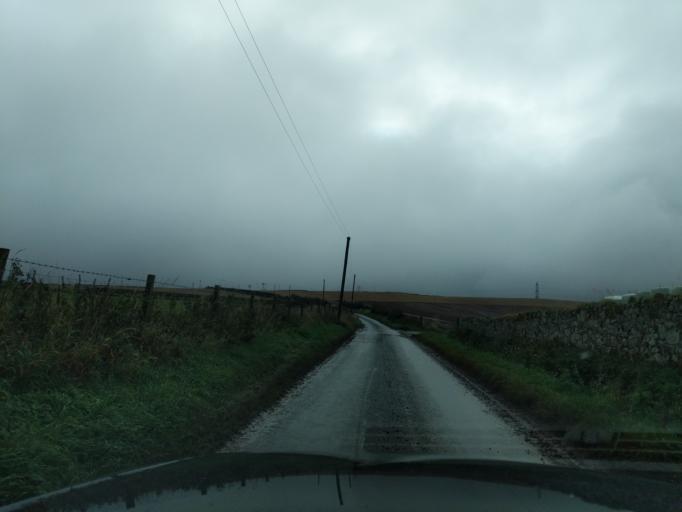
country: GB
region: Scotland
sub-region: East Lothian
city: Dunbar
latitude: 55.9492
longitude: -2.4012
